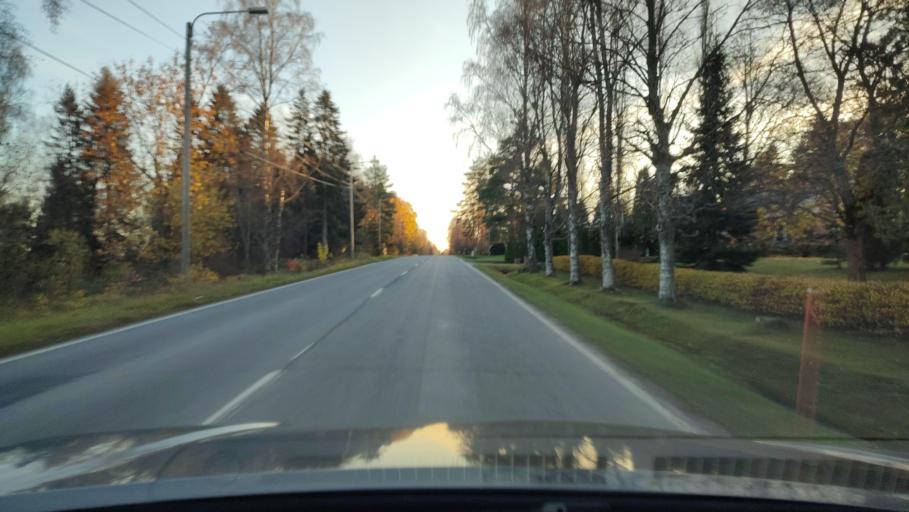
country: FI
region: Ostrobothnia
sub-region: Sydosterbotten
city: Naerpes
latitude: 62.5020
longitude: 21.3512
